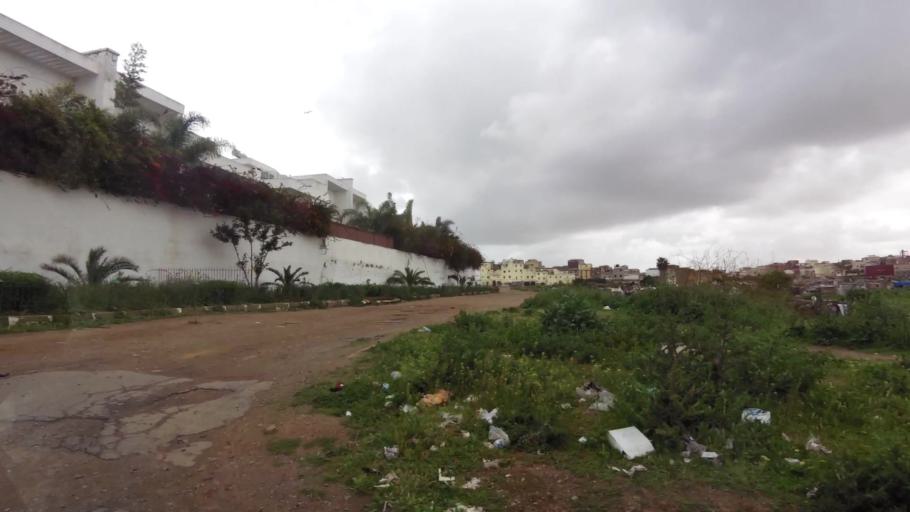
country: MA
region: Grand Casablanca
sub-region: Casablanca
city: Casablanca
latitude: 33.5683
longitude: -7.6937
